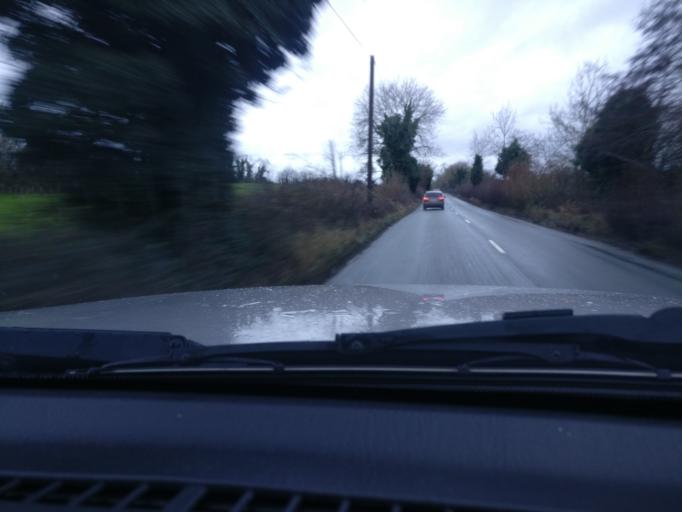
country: IE
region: Leinster
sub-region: An Mhi
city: Longwood
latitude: 53.4777
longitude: -6.9006
